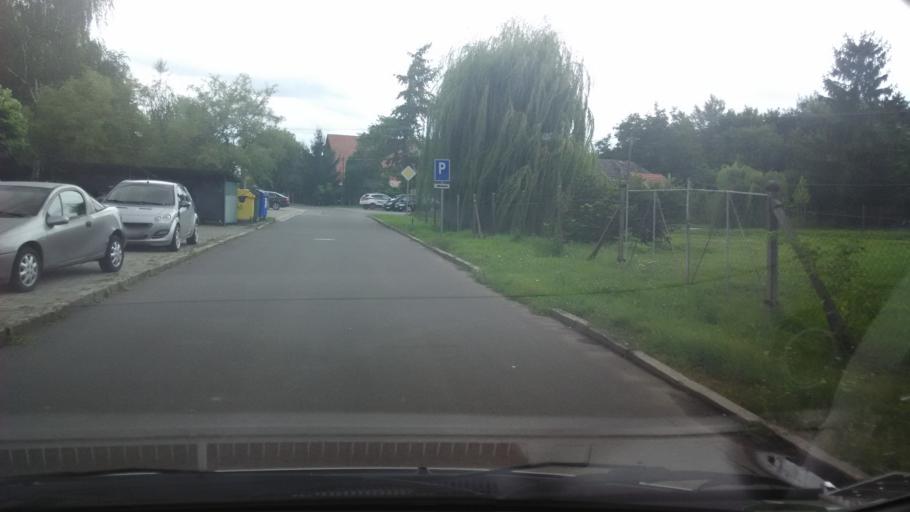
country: SK
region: Nitriansky
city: Levice
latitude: 48.1968
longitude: 18.5223
